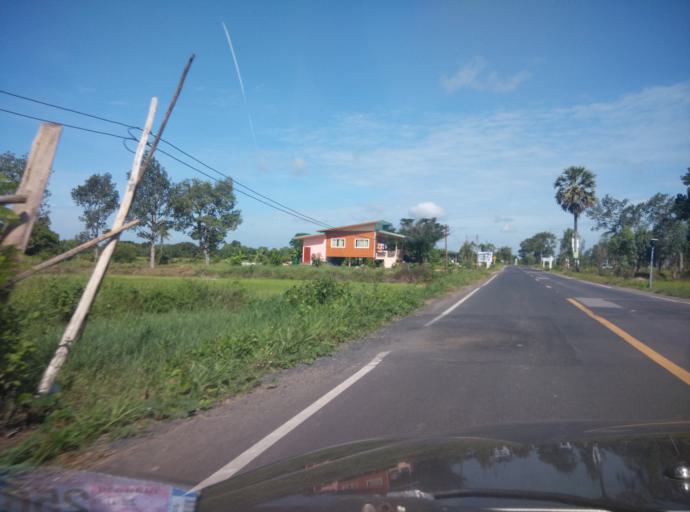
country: TH
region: Sisaket
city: Si Sa Ket
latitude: 15.1235
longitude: 104.2486
